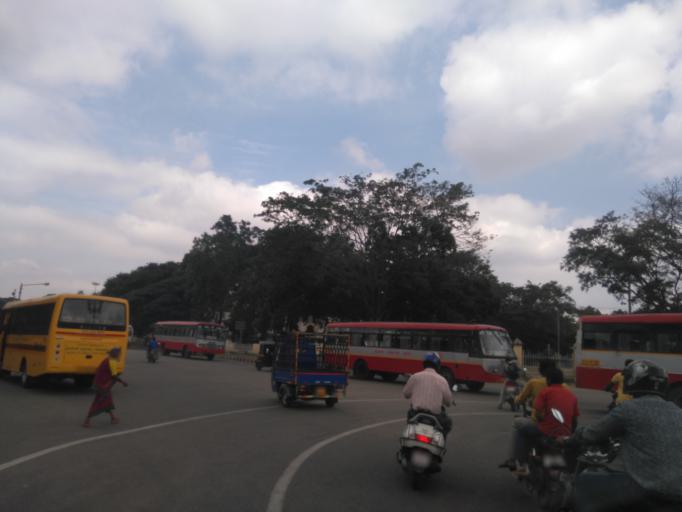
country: IN
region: Karnataka
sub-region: Mysore
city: Mysore
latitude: 12.3017
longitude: 76.6552
